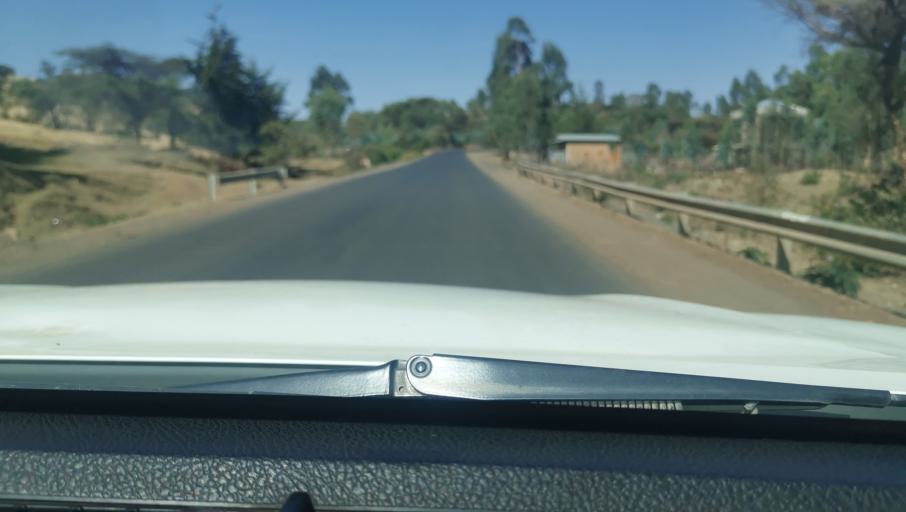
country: ET
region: Oromiya
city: Gedo
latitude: 8.9662
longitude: 37.5254
